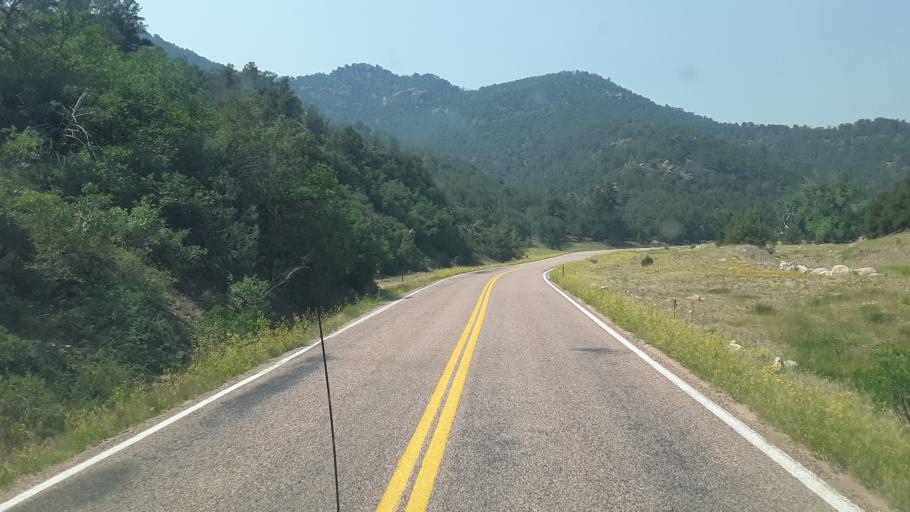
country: US
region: Colorado
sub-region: Fremont County
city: Canon City
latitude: 38.4149
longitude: -105.4139
